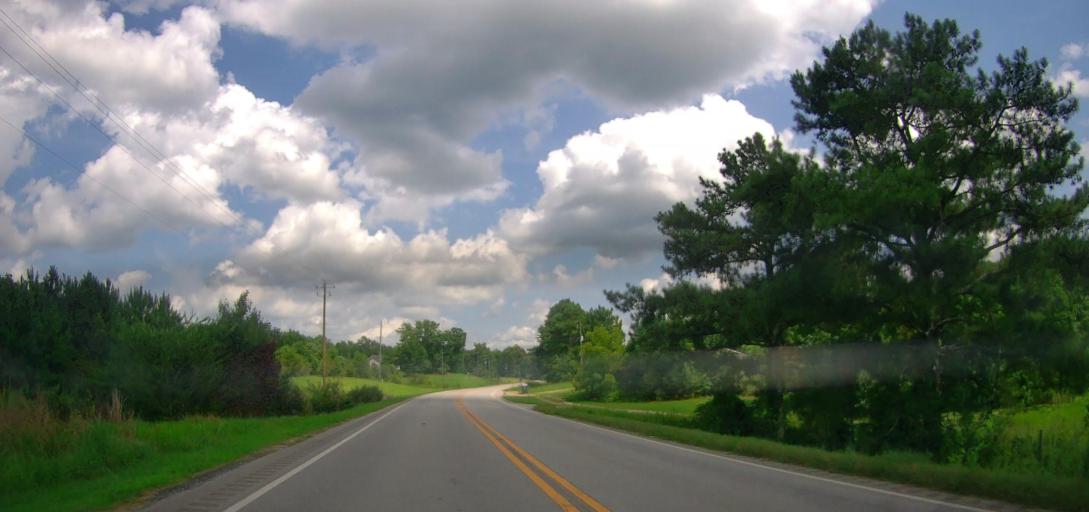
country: US
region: Alabama
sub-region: Cleburne County
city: Heflin
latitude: 33.5737
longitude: -85.4506
